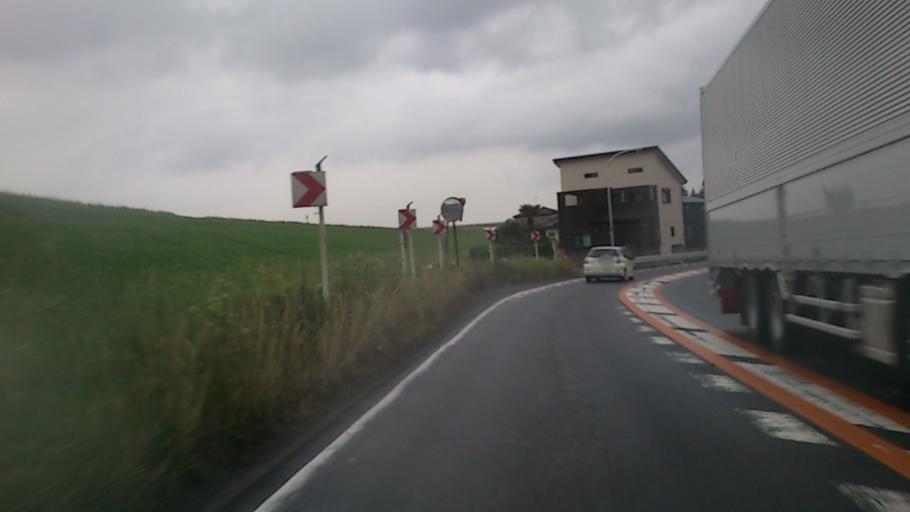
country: JP
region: Ibaraki
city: Sakai
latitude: 36.1139
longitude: 139.7767
